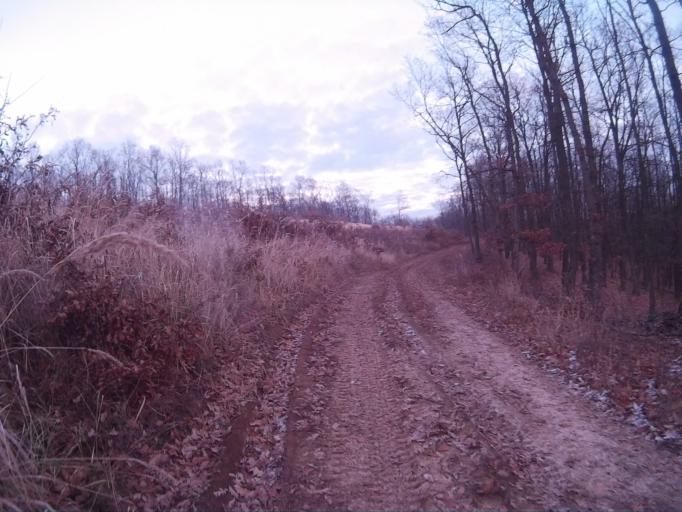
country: HU
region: Nograd
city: Rimoc
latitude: 47.9993
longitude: 19.4584
